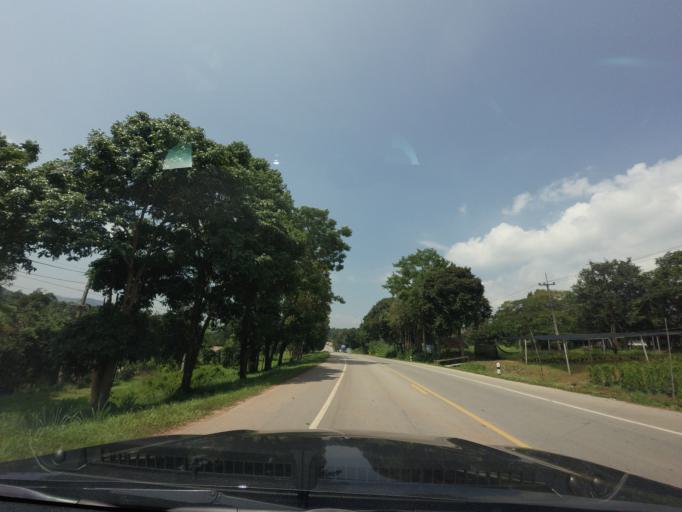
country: TH
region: Loei
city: Phu Ruea
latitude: 17.4585
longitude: 101.3845
